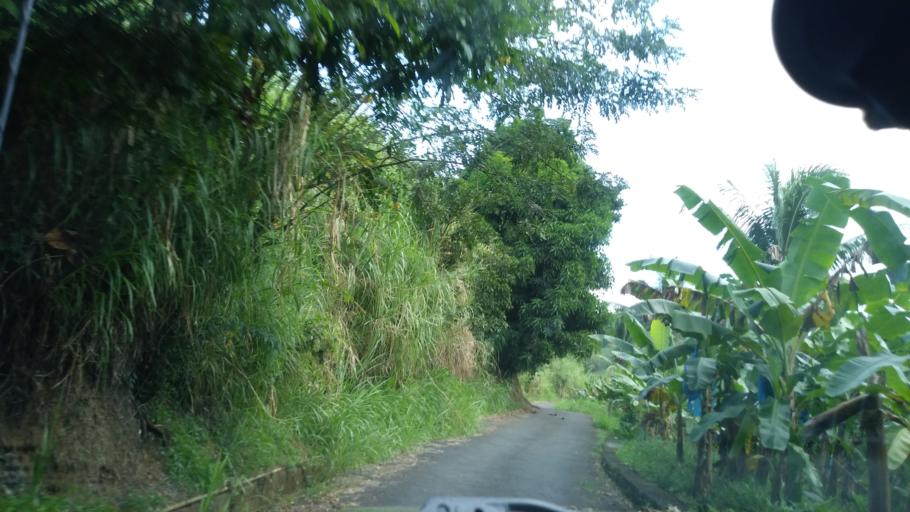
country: VC
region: Charlotte
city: Byera Village
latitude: 13.2321
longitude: -61.1356
